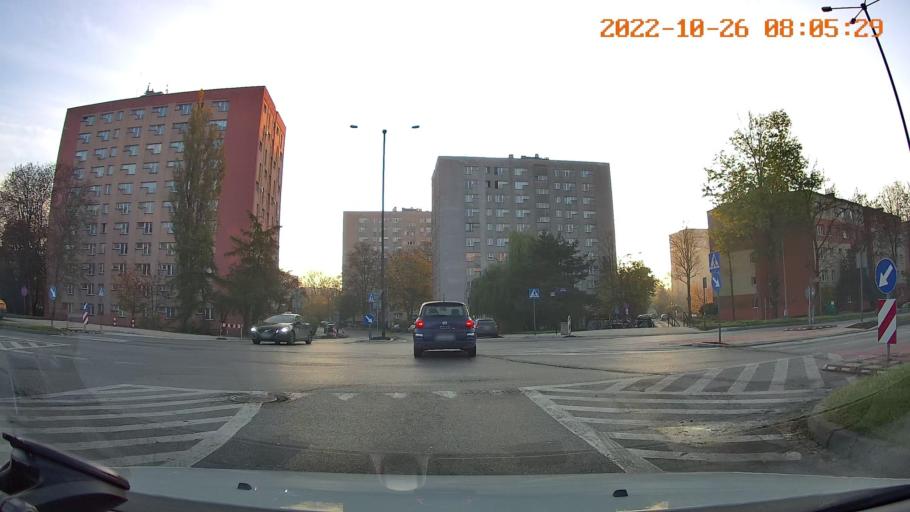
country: PL
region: Lesser Poland Voivodeship
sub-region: Powiat krakowski
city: Zielonki
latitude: 50.0883
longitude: 19.9095
